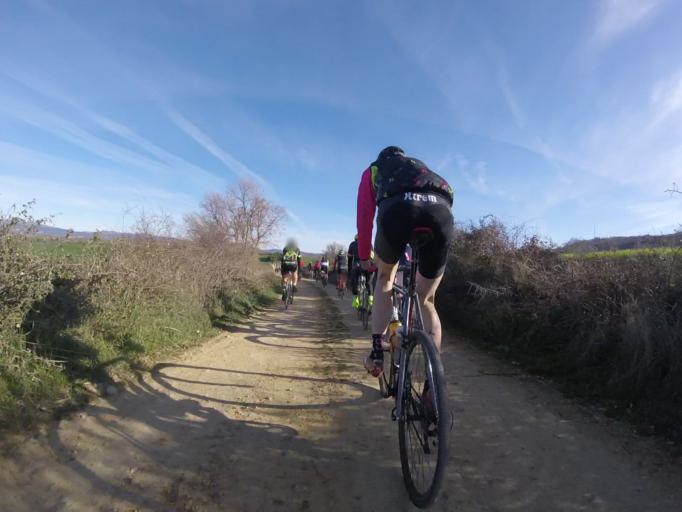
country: ES
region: Navarre
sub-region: Provincia de Navarra
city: Villatuerta
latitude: 42.6585
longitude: -1.9668
